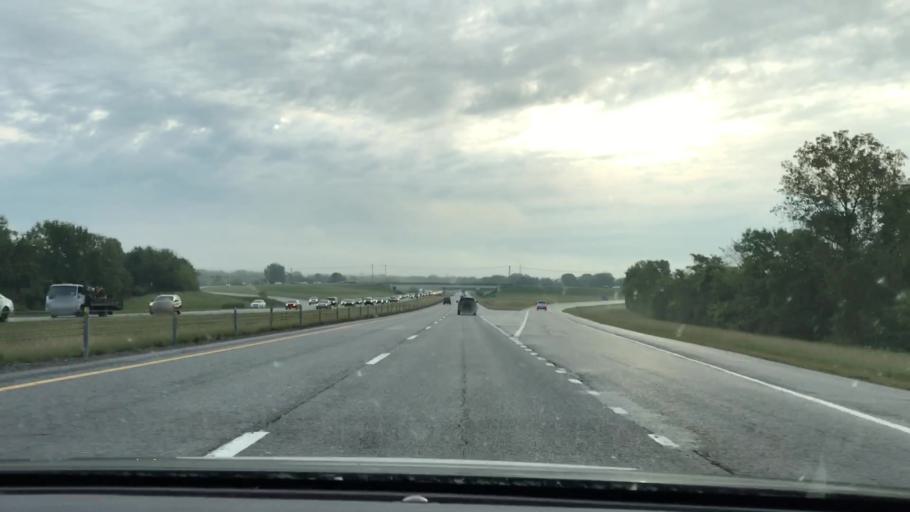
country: US
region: Tennessee
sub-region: Sumner County
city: Hendersonville
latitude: 36.3303
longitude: -86.6249
